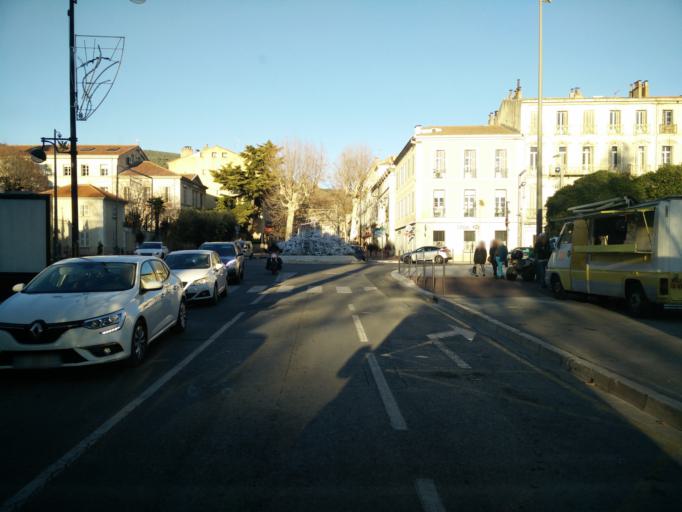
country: FR
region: Provence-Alpes-Cote d'Azur
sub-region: Departement du Var
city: Draguignan
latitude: 43.5375
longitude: 6.4615
